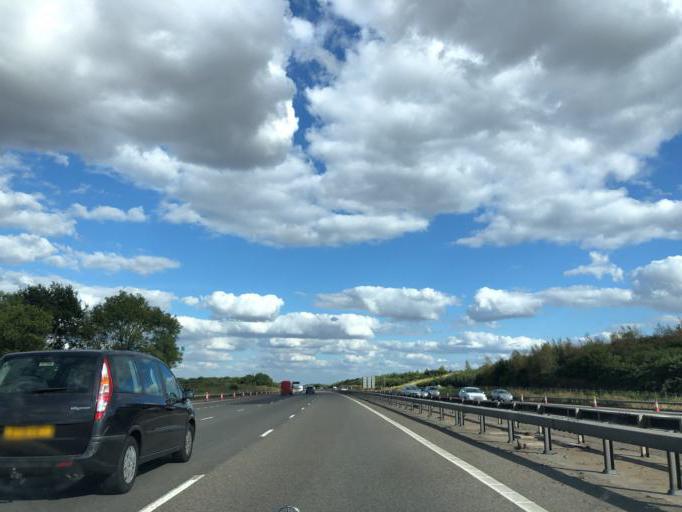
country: GB
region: England
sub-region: Milton Keynes
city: Broughton
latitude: 52.0576
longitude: -0.6971
